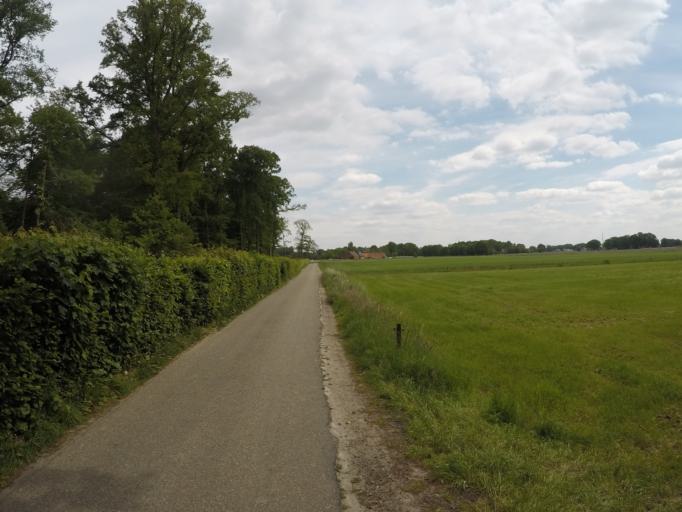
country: BE
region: Flanders
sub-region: Provincie Antwerpen
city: Oostmalle
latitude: 51.3063
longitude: 4.6976
